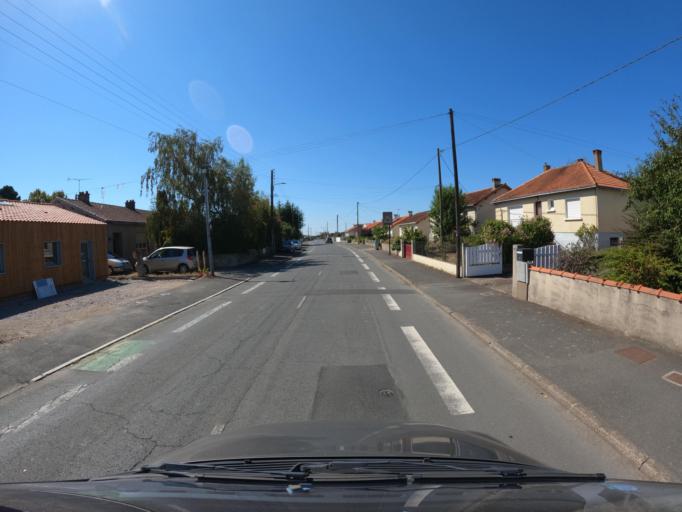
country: FR
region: Pays de la Loire
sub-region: Departement de la Vendee
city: Montaigu
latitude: 46.9686
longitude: -1.3039
